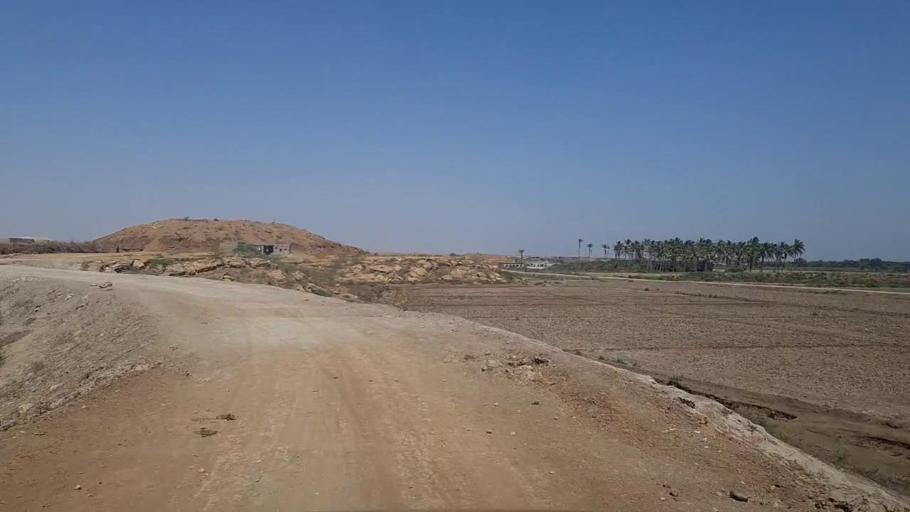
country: PK
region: Sindh
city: Thatta
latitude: 24.8081
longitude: 68.0061
